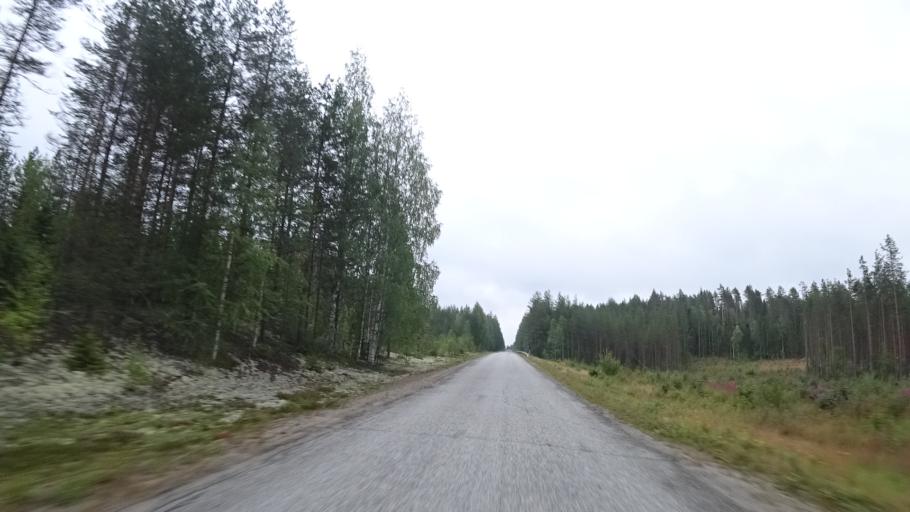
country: FI
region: North Karelia
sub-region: Joensuu
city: Ilomantsi
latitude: 63.2288
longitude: 30.8137
